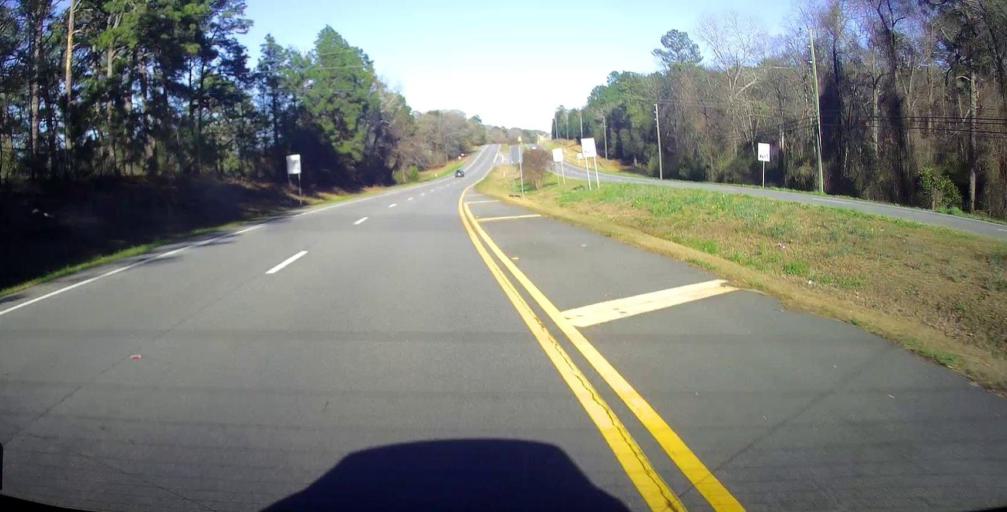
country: US
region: Georgia
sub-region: Peach County
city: Fort Valley
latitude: 32.5828
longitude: -83.8616
